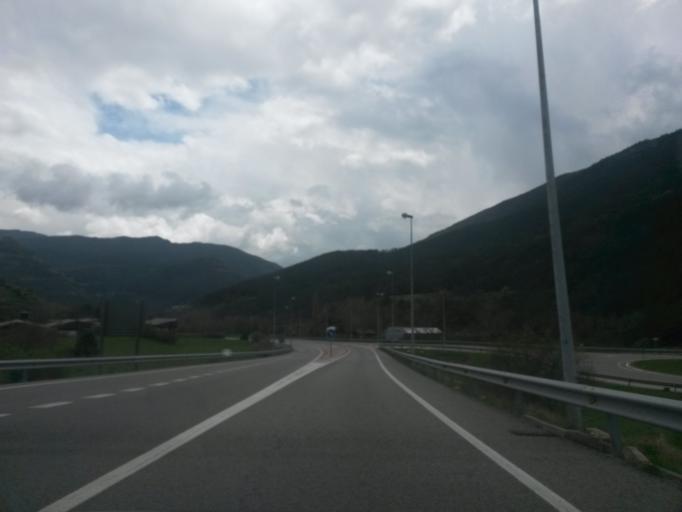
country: ES
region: Catalonia
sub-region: Provincia de Barcelona
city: Baga
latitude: 42.2475
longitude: 1.8690
